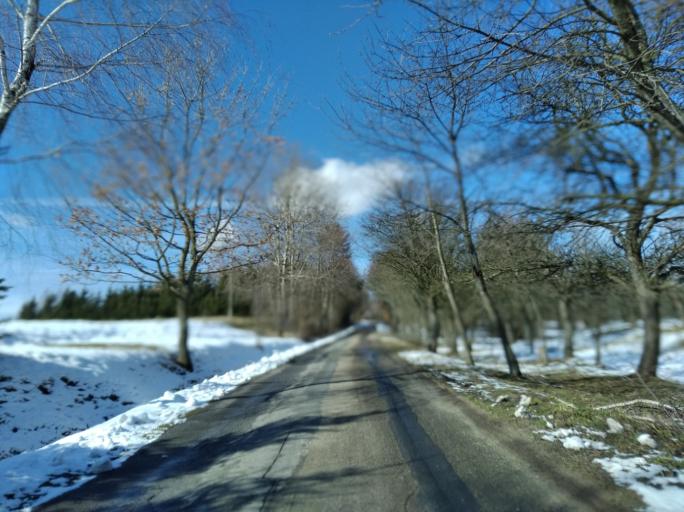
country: PL
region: Subcarpathian Voivodeship
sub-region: Powiat brzozowski
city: Jablonica Polska
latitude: 49.7287
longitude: 21.8711
